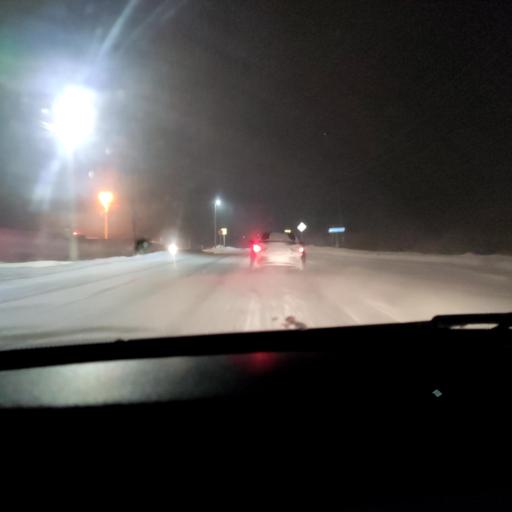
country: RU
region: Perm
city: Kultayevo
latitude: 57.8611
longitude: 55.9127
